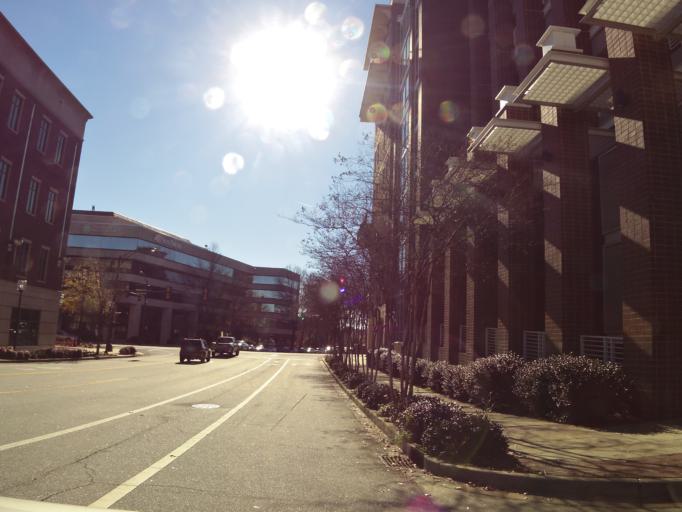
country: US
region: South Carolina
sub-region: Greenville County
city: Greenville
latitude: 34.8497
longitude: -82.3977
